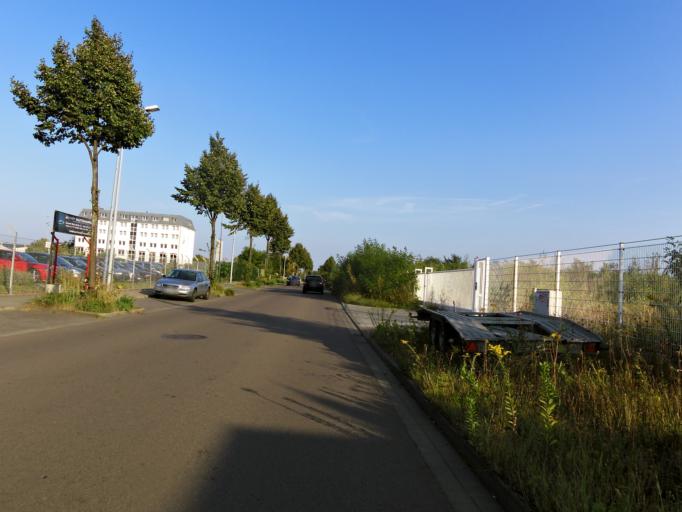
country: DE
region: Saxony
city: Leipzig
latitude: 51.3399
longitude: 12.3017
